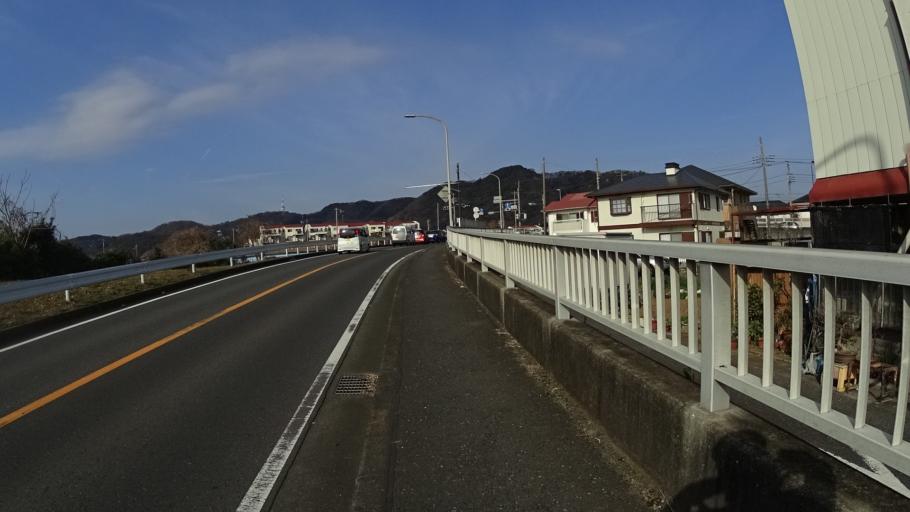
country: JP
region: Kanagawa
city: Hiratsuka
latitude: 35.3164
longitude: 139.3314
